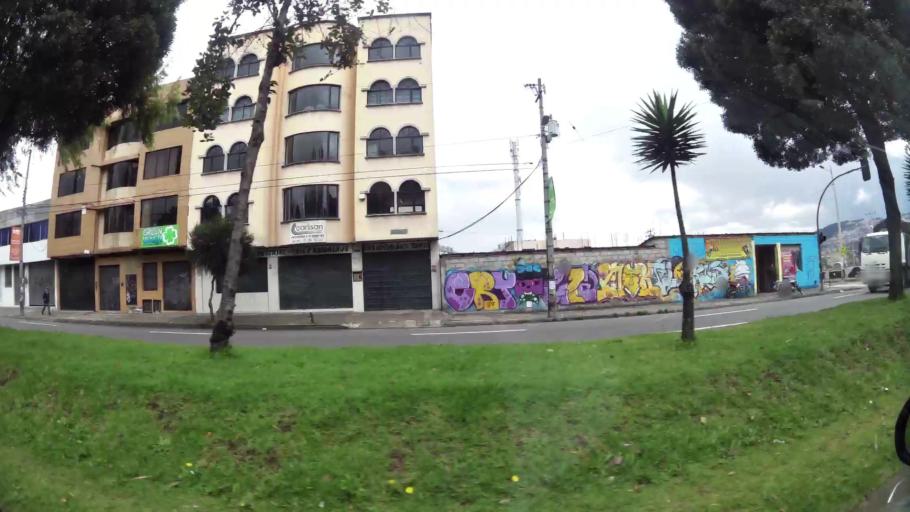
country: EC
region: Pichincha
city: Quito
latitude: -0.2818
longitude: -78.5464
